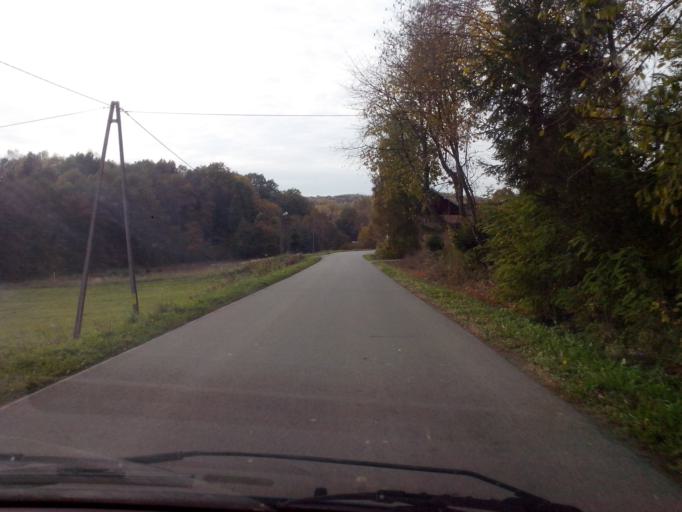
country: PL
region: Subcarpathian Voivodeship
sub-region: Powiat strzyzowski
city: Wisniowa
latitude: 49.8785
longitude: 21.6767
